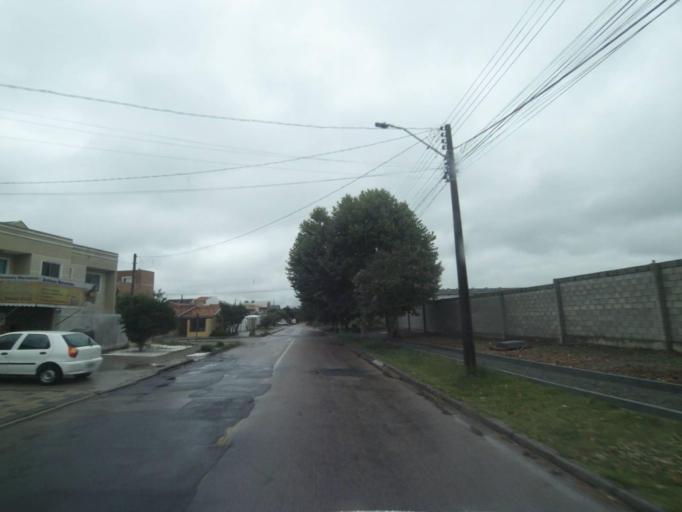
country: BR
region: Parana
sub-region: Araucaria
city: Araucaria
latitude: -25.5387
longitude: -49.3370
